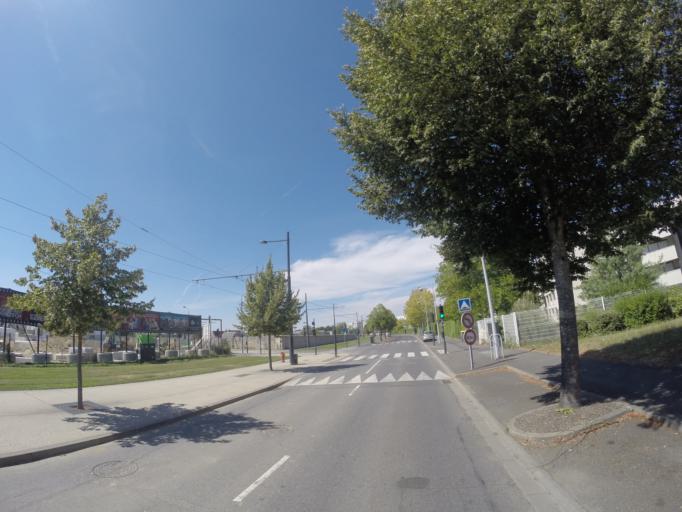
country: FR
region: Centre
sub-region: Departement d'Indre-et-Loire
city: Parcay-Meslay
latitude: 47.4235
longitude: 0.7088
